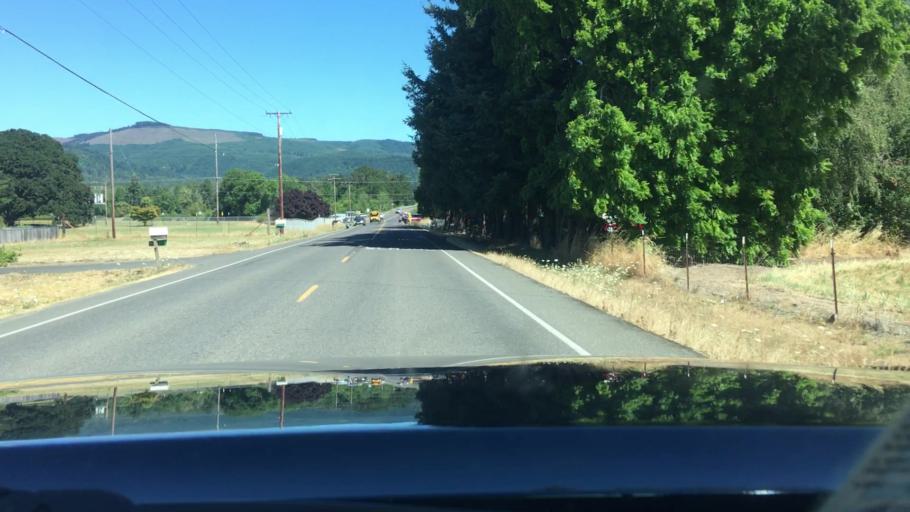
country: US
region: Oregon
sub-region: Lane County
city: Cottage Grove
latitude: 43.8325
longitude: -123.0362
